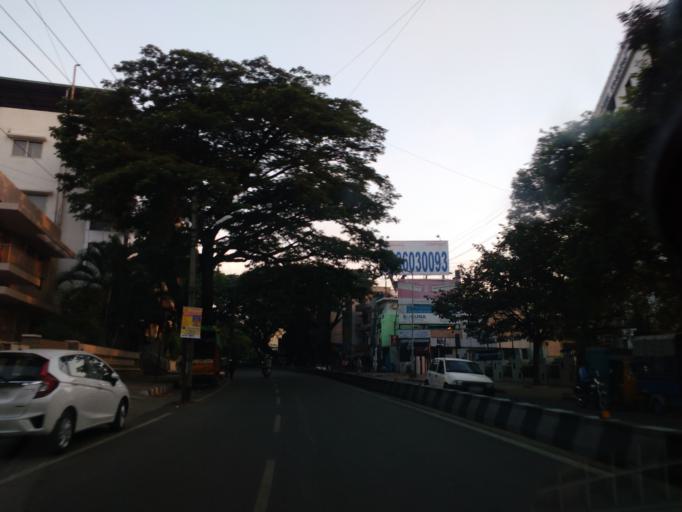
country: IN
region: Karnataka
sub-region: Bangalore Urban
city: Bangalore
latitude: 12.9877
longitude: 77.5597
